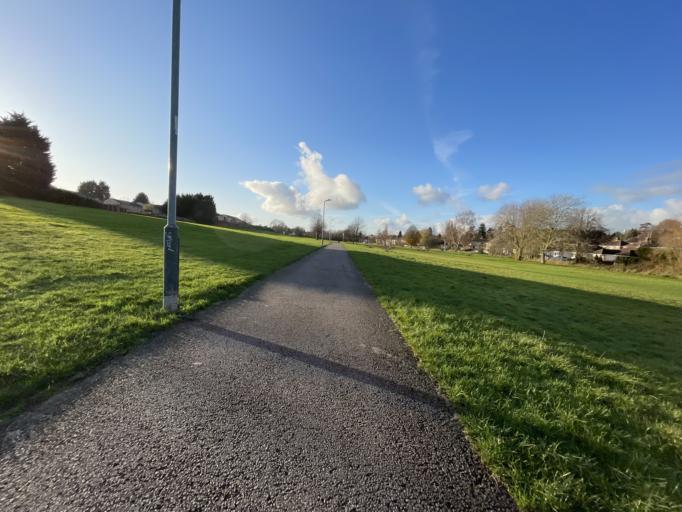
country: GB
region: England
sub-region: Warwickshire
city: Rugby
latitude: 52.3658
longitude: -1.2711
